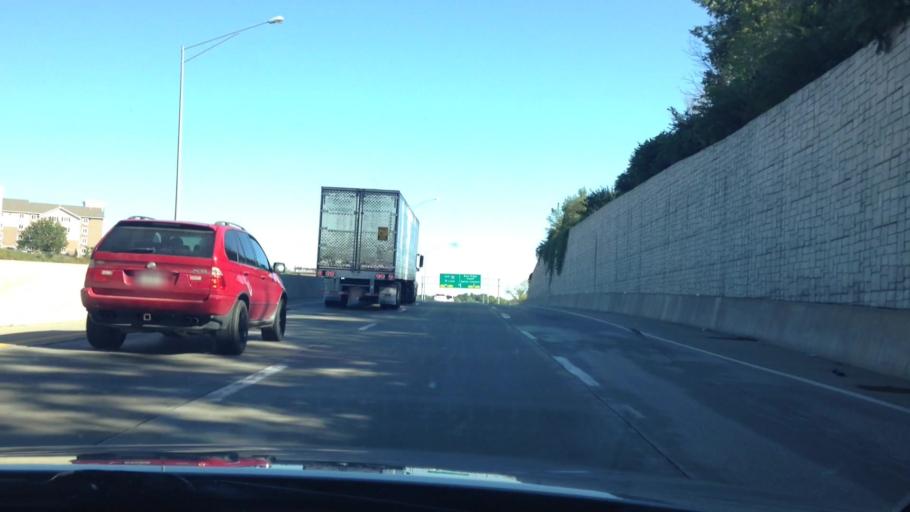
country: US
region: Missouri
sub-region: Jackson County
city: Raytown
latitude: 39.0554
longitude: -94.4830
